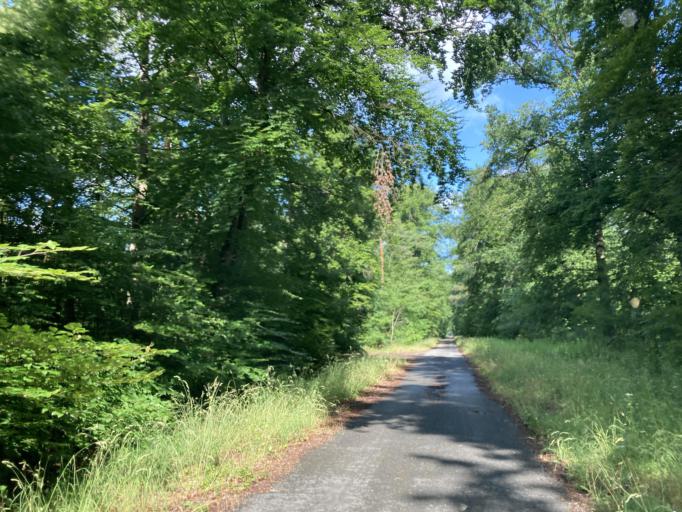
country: DE
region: Baden-Wuerttemberg
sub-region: Karlsruhe Region
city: Karlsdorf-Neuthard
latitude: 49.1576
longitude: 8.5257
